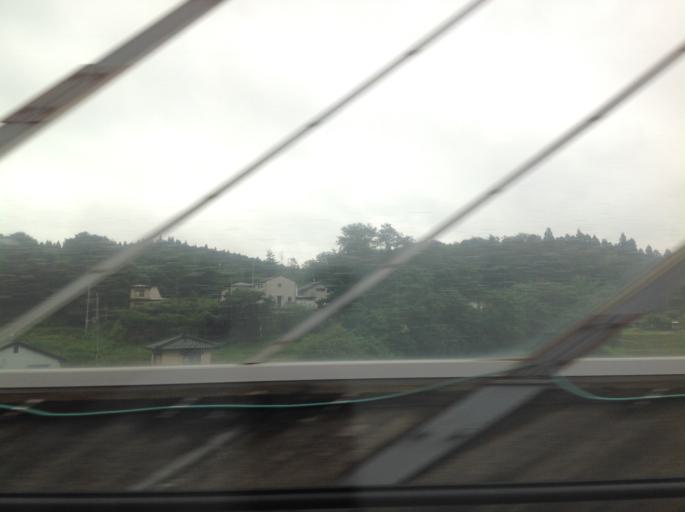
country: JP
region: Iwate
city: Ichinoseki
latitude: 38.9066
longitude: 141.1311
